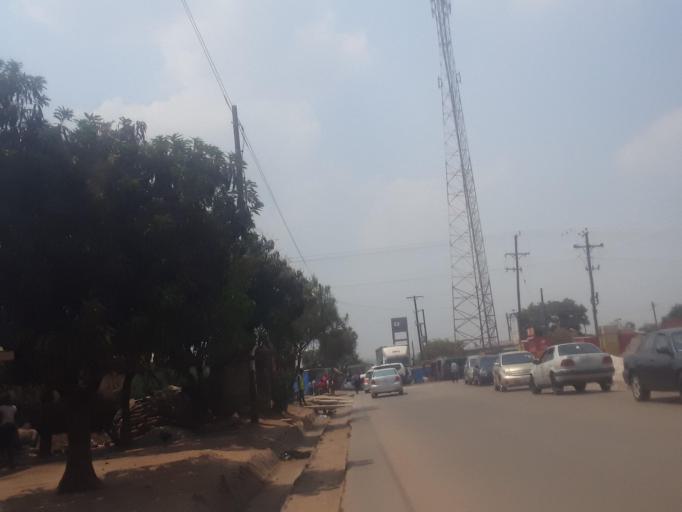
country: ZM
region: Lusaka
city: Lusaka
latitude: -15.3684
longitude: 28.2919
